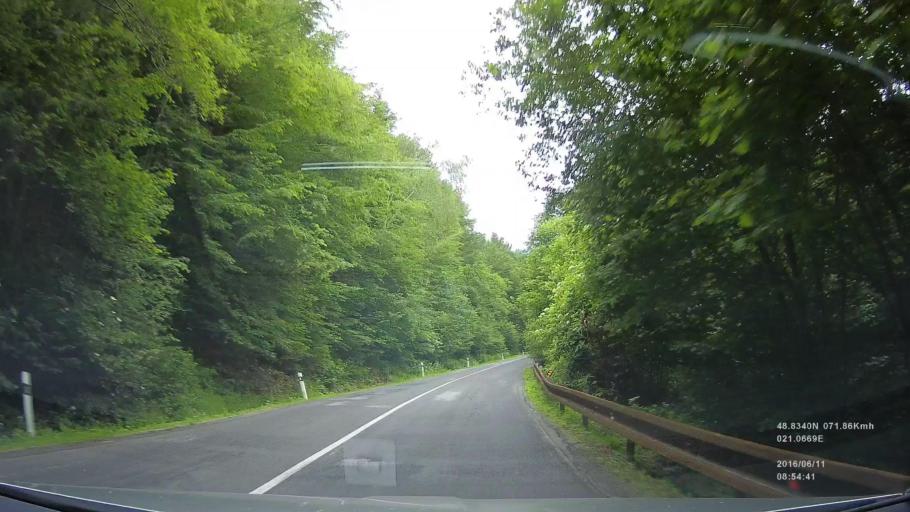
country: SK
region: Kosicky
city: Gelnica
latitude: 48.8047
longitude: 21.1000
